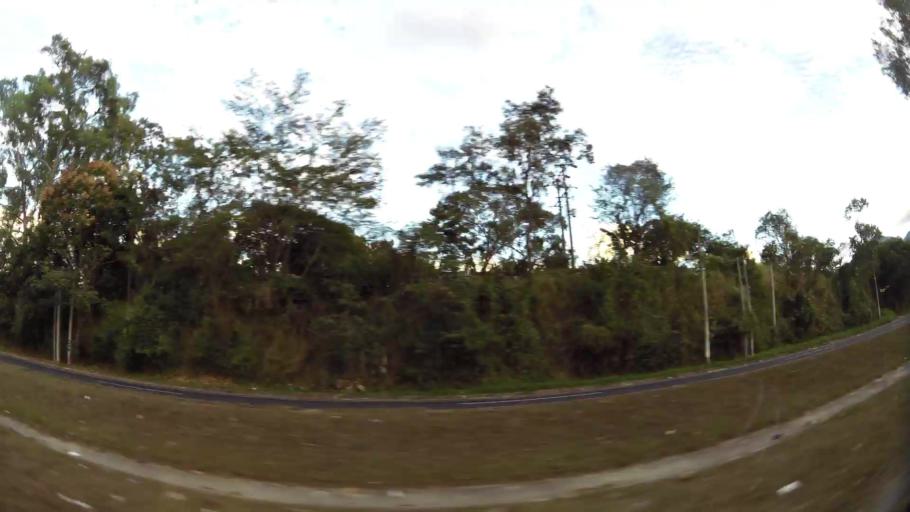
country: SV
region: San Vicente
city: San Sebastian
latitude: 13.6887
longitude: -88.8493
